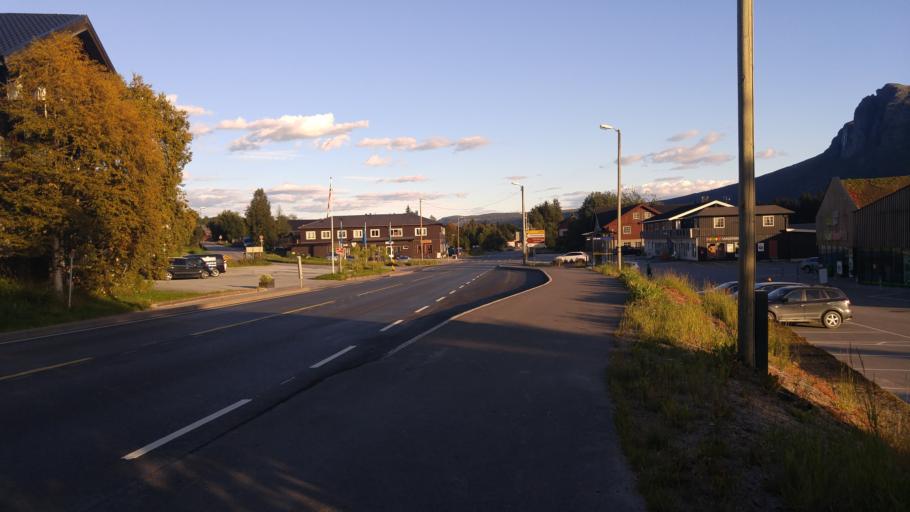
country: NO
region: Buskerud
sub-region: Hemsedal
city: Troim
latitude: 60.8507
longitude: 8.6152
